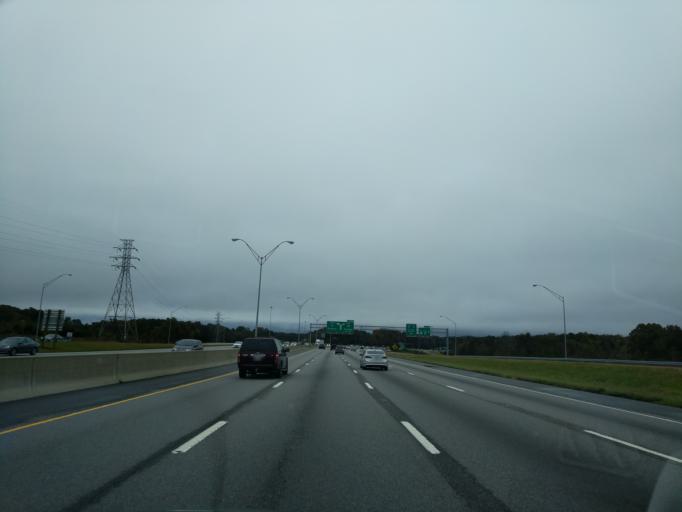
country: US
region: North Carolina
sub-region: Orange County
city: Hillsborough
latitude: 36.0733
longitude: -79.1661
